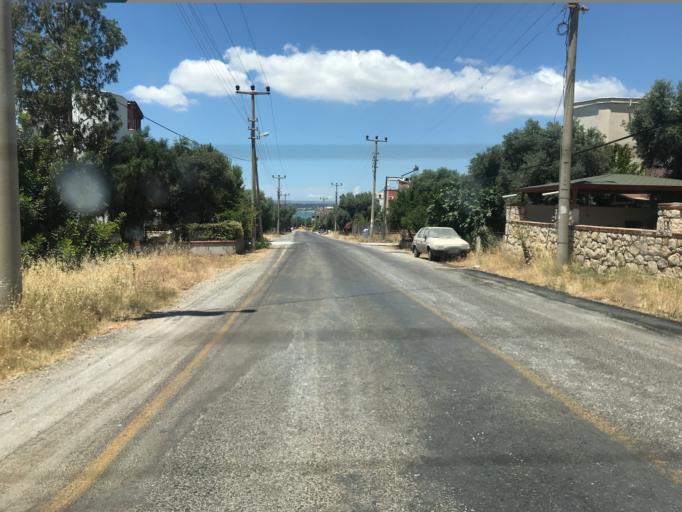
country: TR
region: Aydin
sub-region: Didim
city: Didim
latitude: 37.3996
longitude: 27.4369
